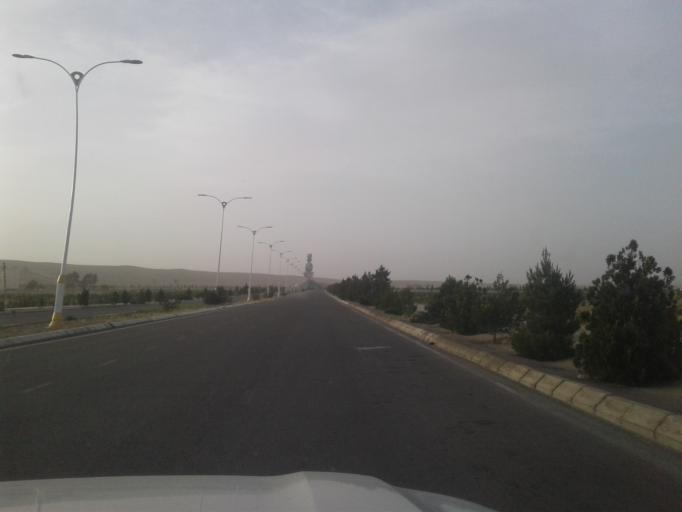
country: TM
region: Balkan
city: Turkmenbasy
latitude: 40.0397
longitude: 52.9819
